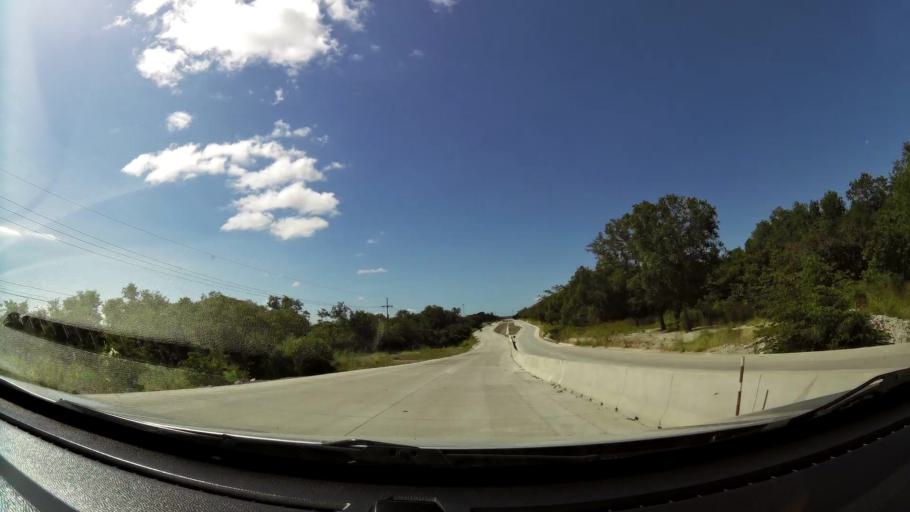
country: CR
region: Guanacaste
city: Bagaces
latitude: 10.5381
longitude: -85.3319
